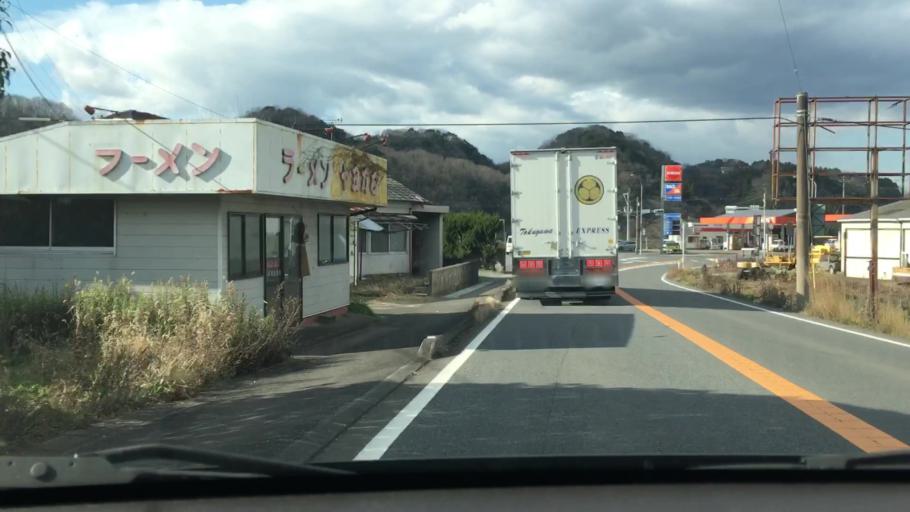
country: JP
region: Oita
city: Usuki
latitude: 33.0322
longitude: 131.6900
